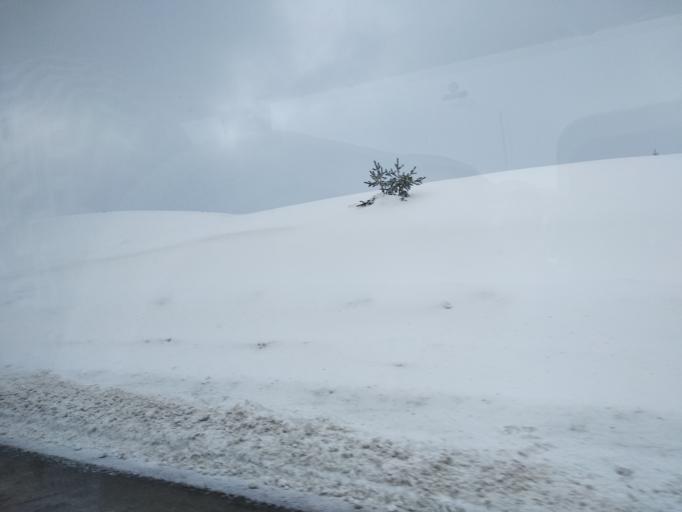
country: TR
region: Erzincan
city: Catalarmut
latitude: 39.8896
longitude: 39.3591
